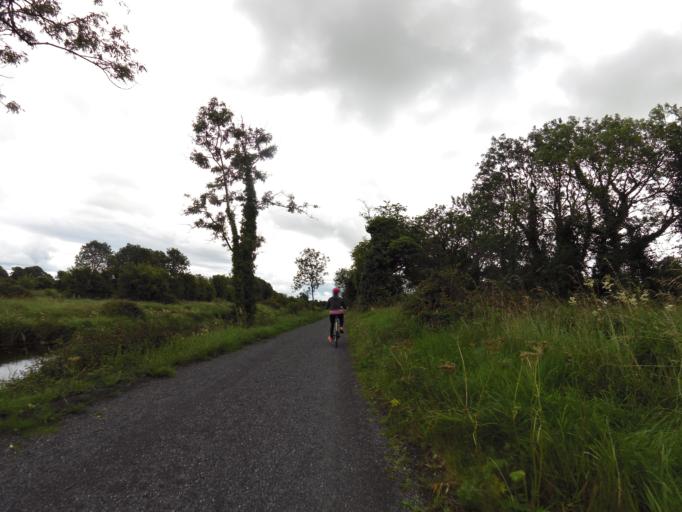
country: IE
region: Leinster
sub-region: An Iarmhi
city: An Muileann gCearr
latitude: 53.5309
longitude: -7.4611
